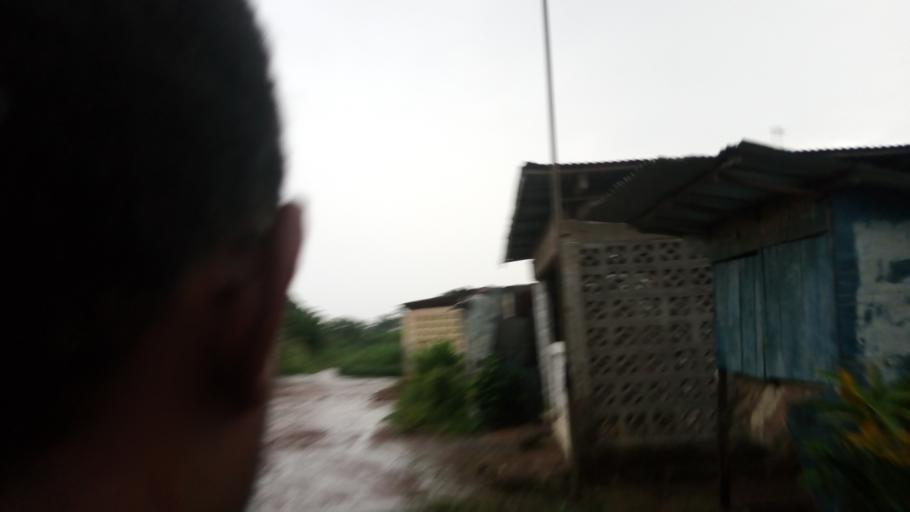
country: SL
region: Northern Province
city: Lunsar
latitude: 8.6952
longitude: -12.5314
